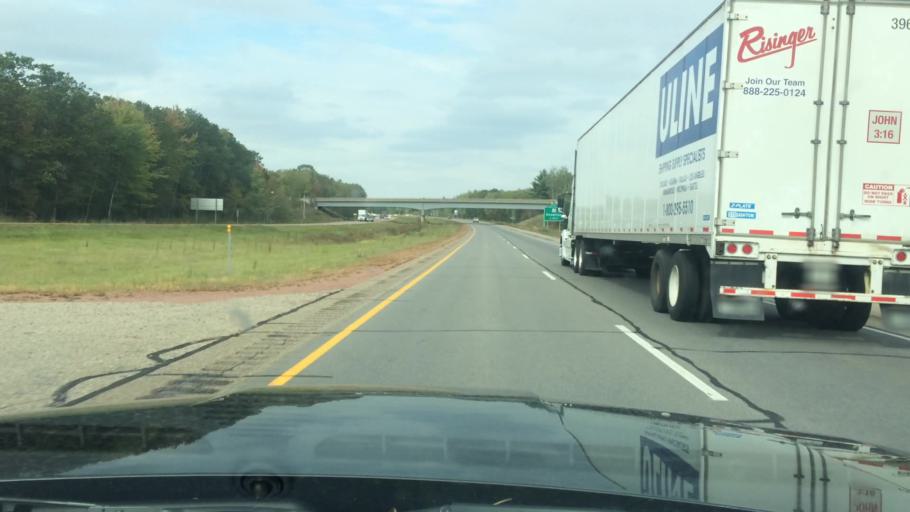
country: US
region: Wisconsin
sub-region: Marathon County
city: Mosinee
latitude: 44.7116
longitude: -89.6583
